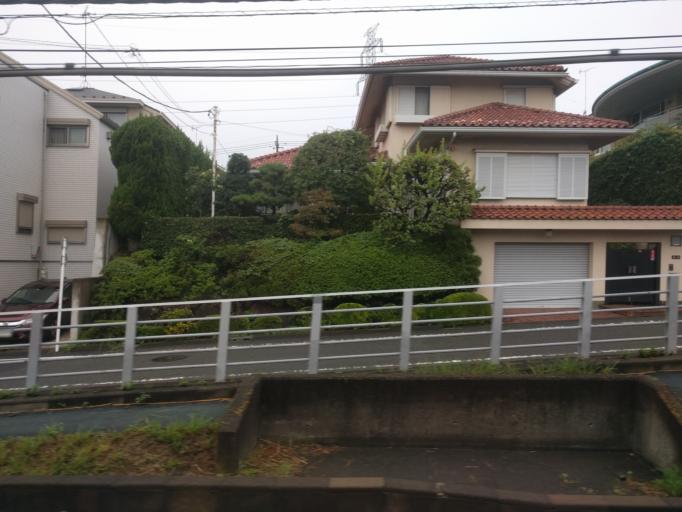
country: JP
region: Tokyo
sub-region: Machida-shi
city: Machida
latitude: 35.5253
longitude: 139.4845
